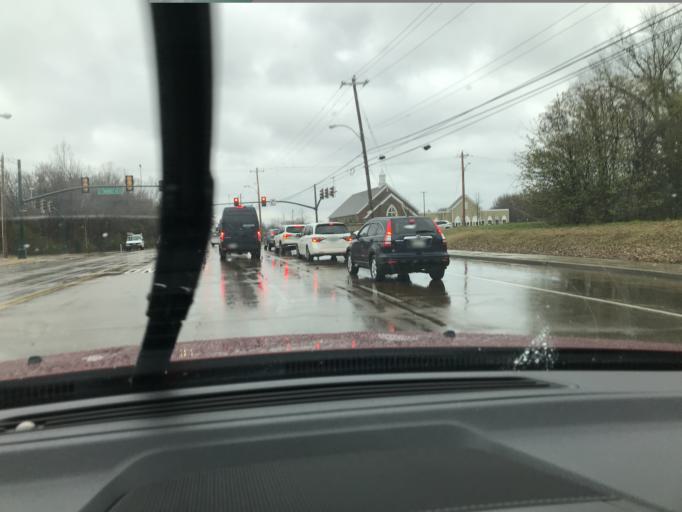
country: US
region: Tennessee
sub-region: Shelby County
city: Collierville
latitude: 35.0531
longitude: -89.6862
